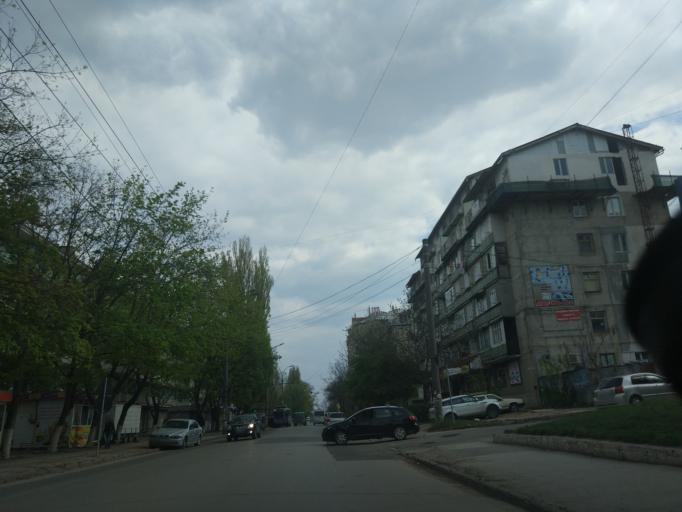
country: MD
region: Chisinau
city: Chisinau
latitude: 46.9874
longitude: 28.8722
